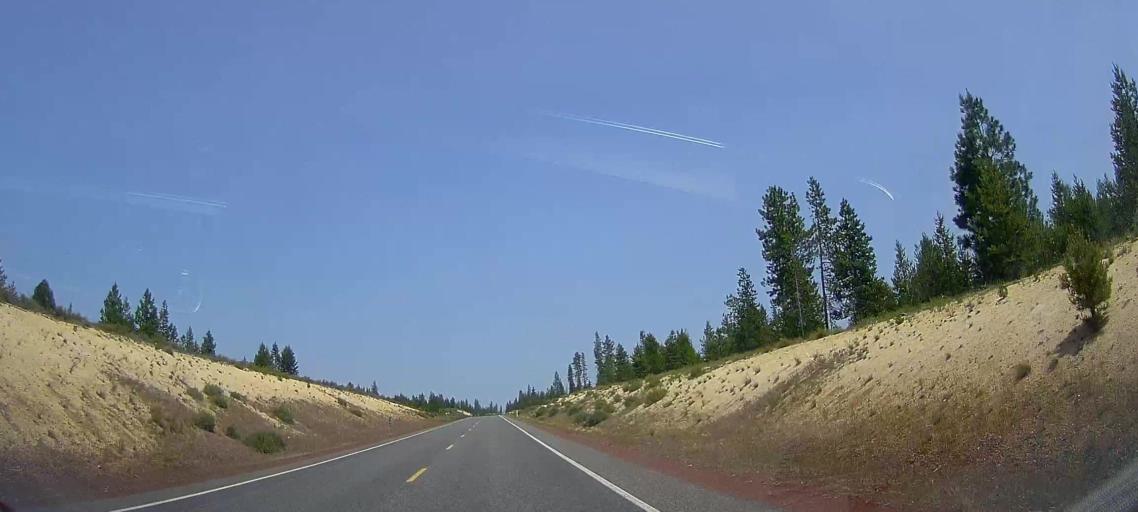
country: US
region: Oregon
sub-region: Deschutes County
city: La Pine
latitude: 43.4016
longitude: -121.7245
